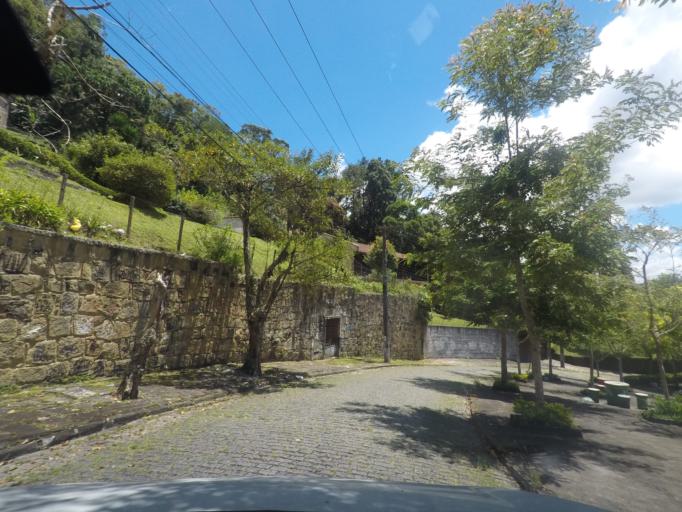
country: BR
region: Rio de Janeiro
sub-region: Teresopolis
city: Teresopolis
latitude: -22.4292
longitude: -42.9834
